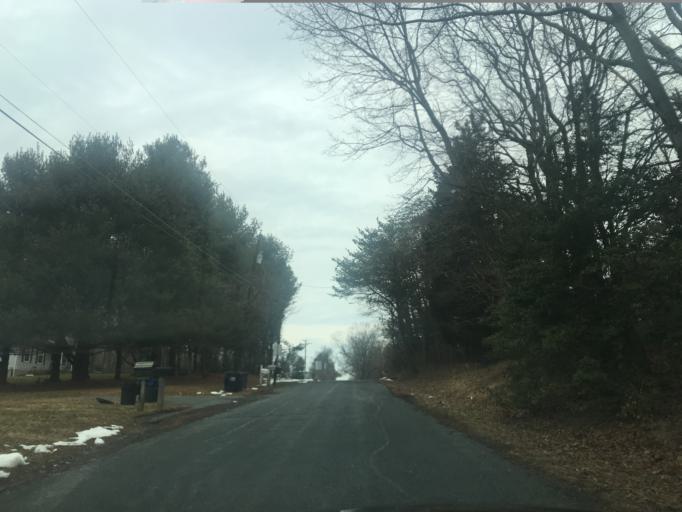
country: US
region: Maryland
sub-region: Harford County
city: Jarrettsville
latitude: 39.7026
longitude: -76.5010
